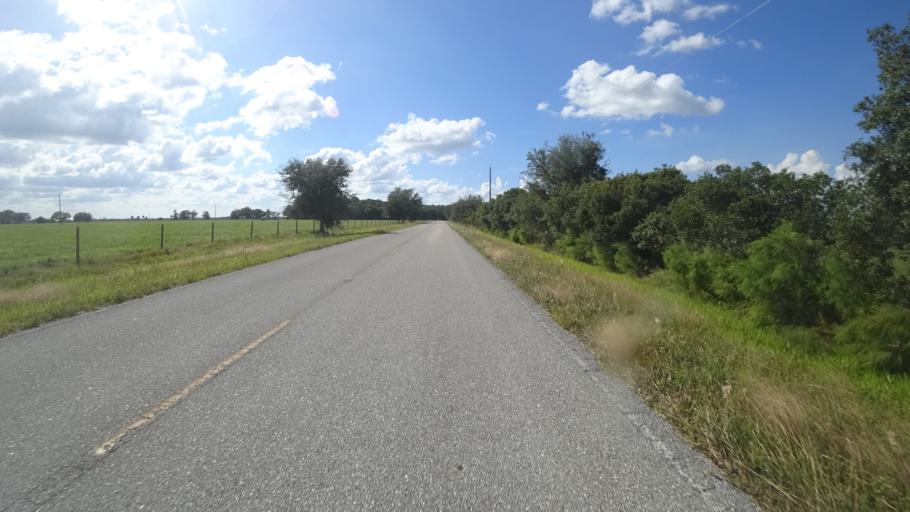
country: US
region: Florida
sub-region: DeSoto County
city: Nocatee
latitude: 27.2733
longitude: -82.0731
